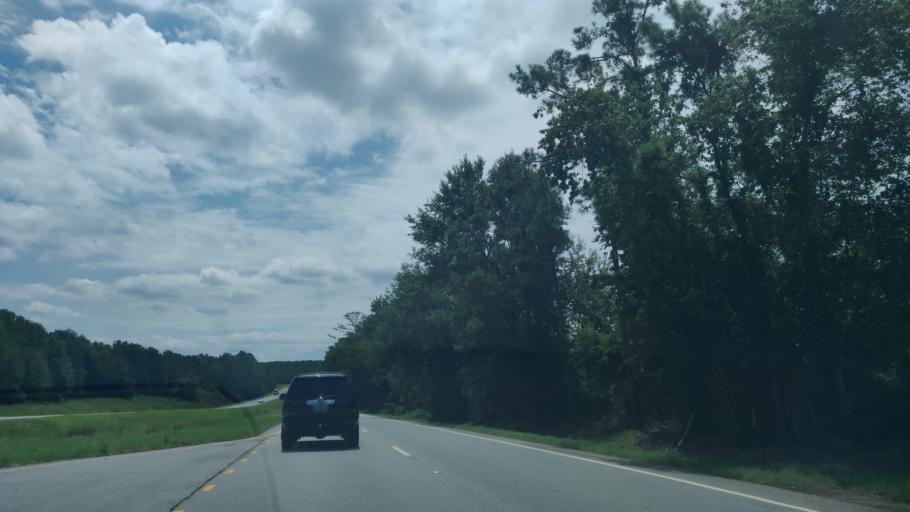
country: US
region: Georgia
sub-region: Terrell County
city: Dawson
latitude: 31.8714
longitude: -84.4922
